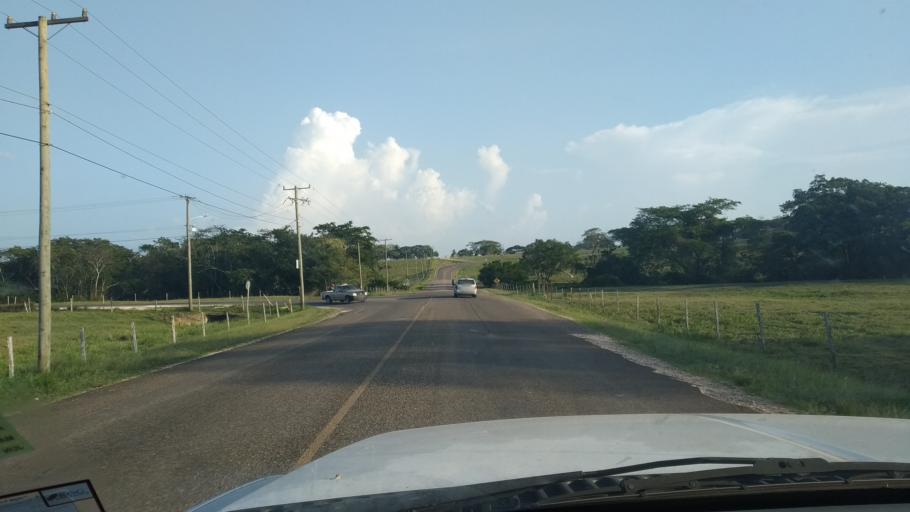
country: BZ
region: Cayo
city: San Ignacio
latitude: 17.2487
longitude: -88.9874
